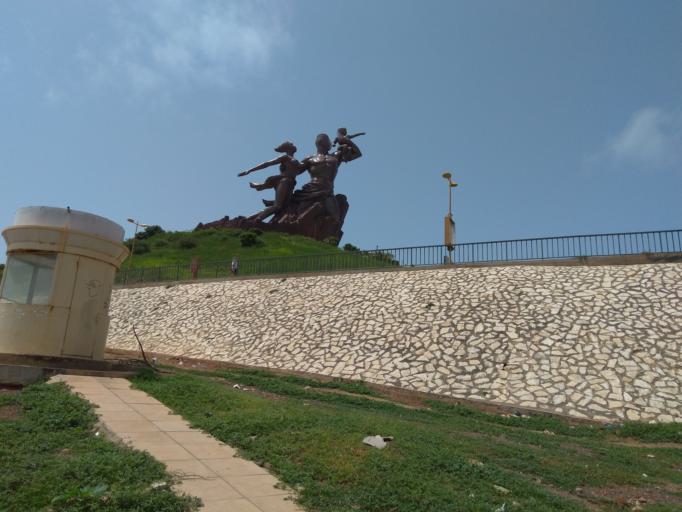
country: SN
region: Dakar
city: Mermoz Boabab
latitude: 14.7235
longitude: -17.4943
